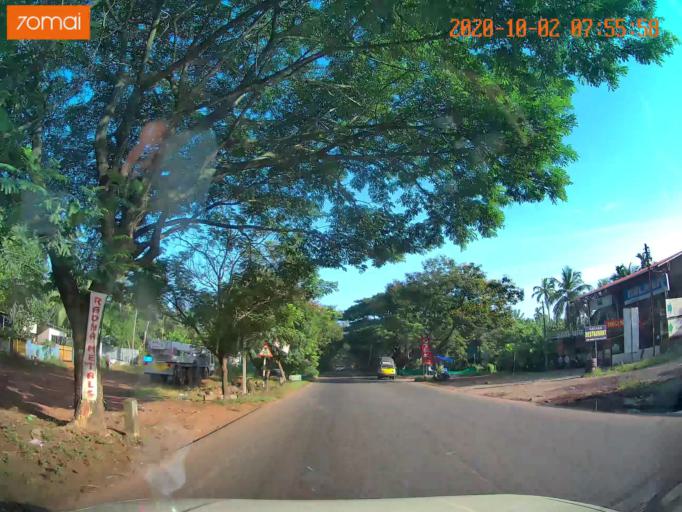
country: IN
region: Kerala
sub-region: Kozhikode
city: Ferokh
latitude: 11.1869
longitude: 75.8705
